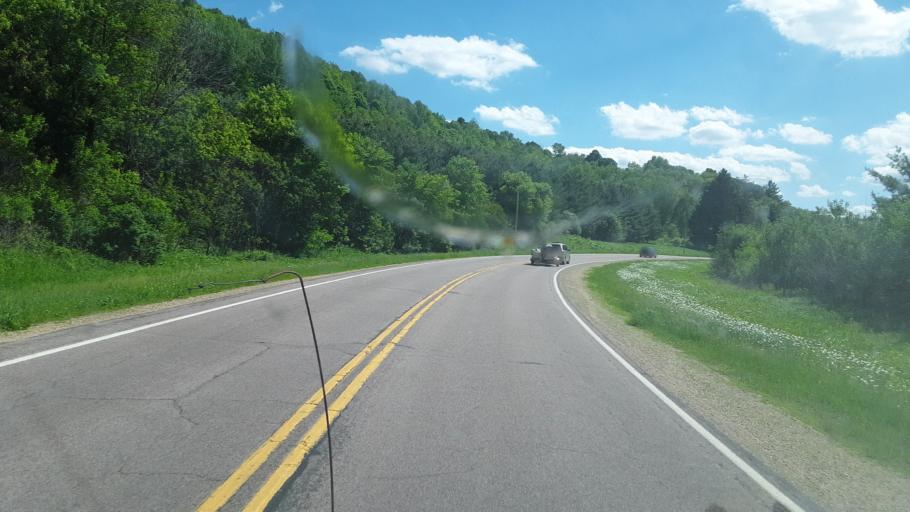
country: US
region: Wisconsin
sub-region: Richland County
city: Richland Center
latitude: 43.3912
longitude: -90.2416
